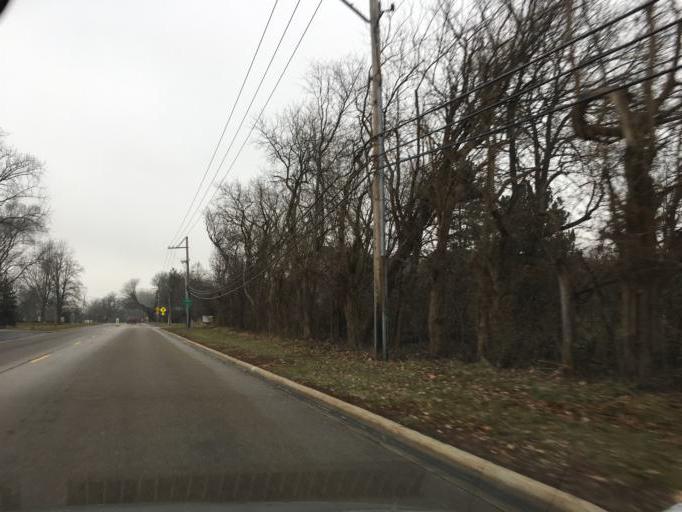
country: US
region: Illinois
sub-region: McHenry County
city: Lakewood
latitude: 42.2190
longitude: -88.3443
